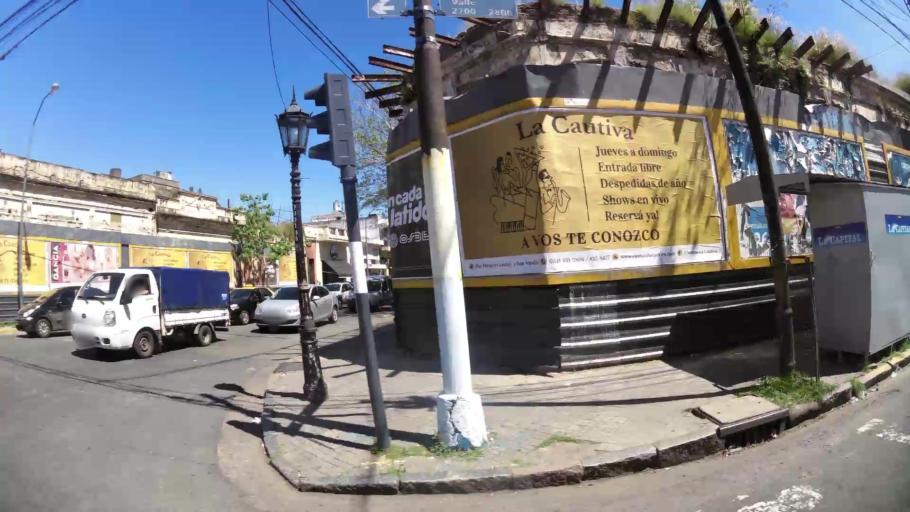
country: AR
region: Santa Fe
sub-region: Departamento de Rosario
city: Rosario
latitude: -32.9310
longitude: -60.6573
